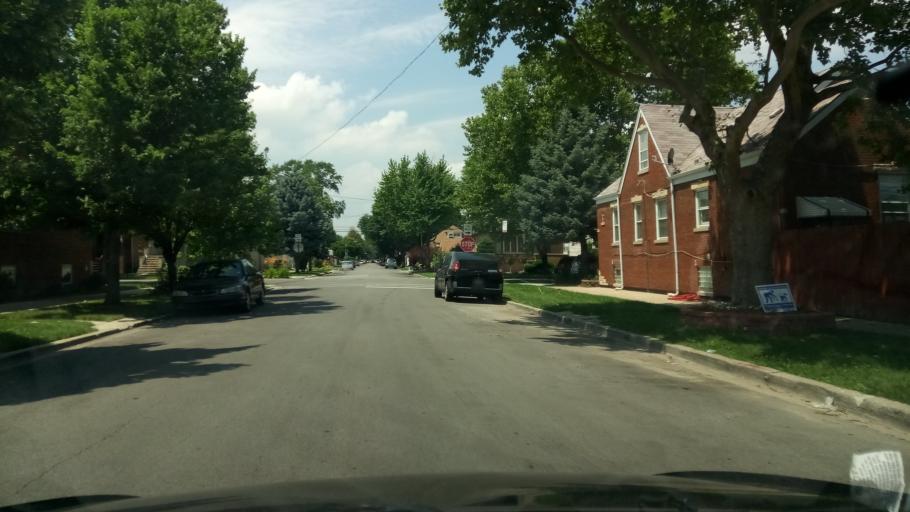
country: US
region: Illinois
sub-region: Cook County
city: Hometown
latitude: 41.7809
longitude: -87.7231
